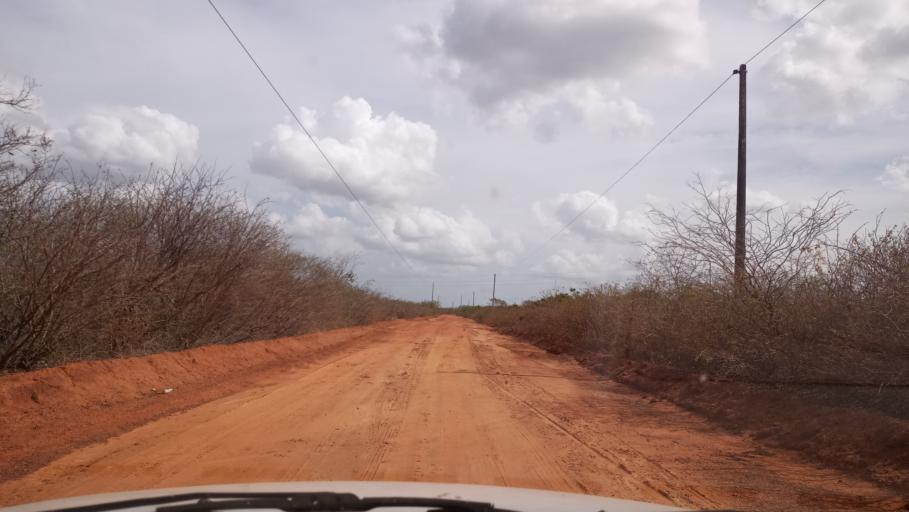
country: BR
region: Rio Grande do Norte
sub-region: Joao Camara
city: Joao Camara
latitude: -5.4740
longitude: -35.8275
